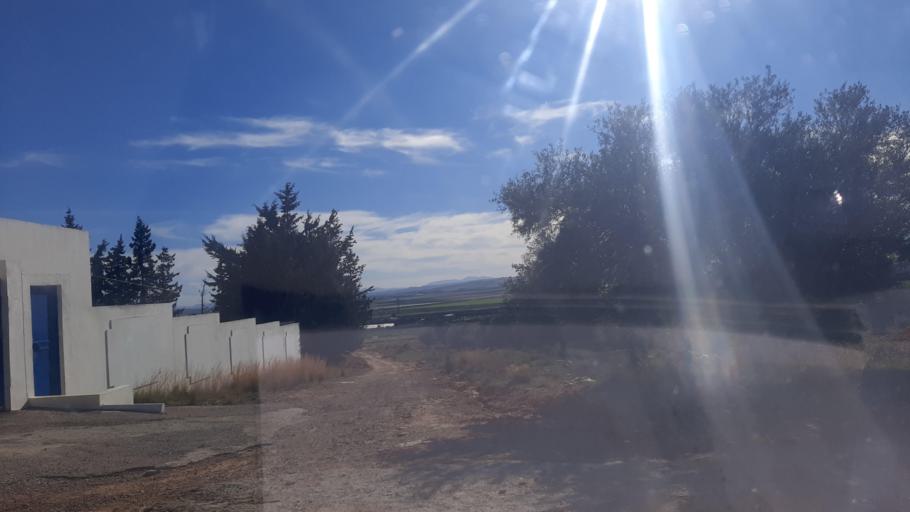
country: TN
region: Tunis
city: Oued Lill
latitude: 36.7657
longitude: 9.9855
